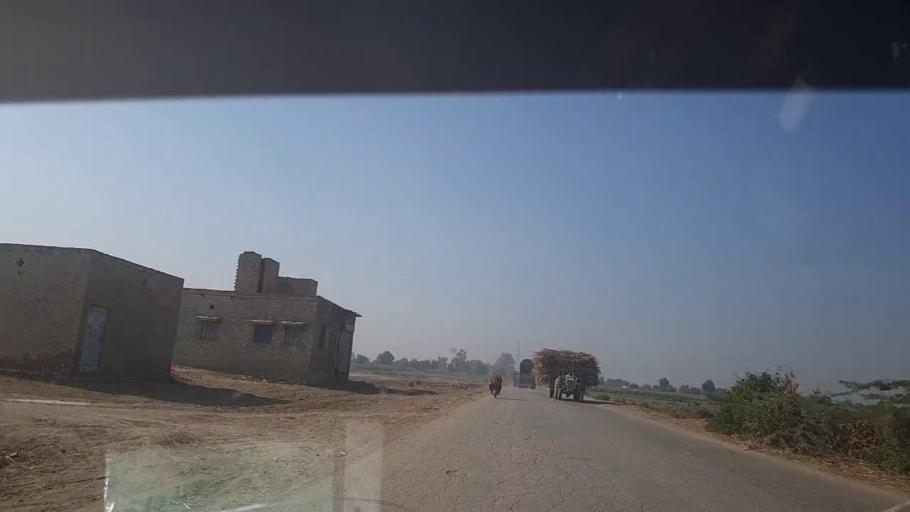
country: PK
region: Sindh
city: Kot Diji
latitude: 27.4362
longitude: 68.6405
